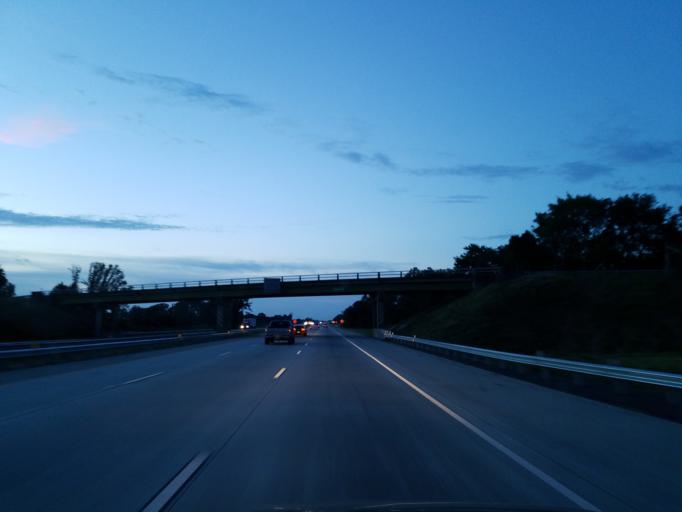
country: US
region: Georgia
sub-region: Dooly County
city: Vienna
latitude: 32.0589
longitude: -83.7634
